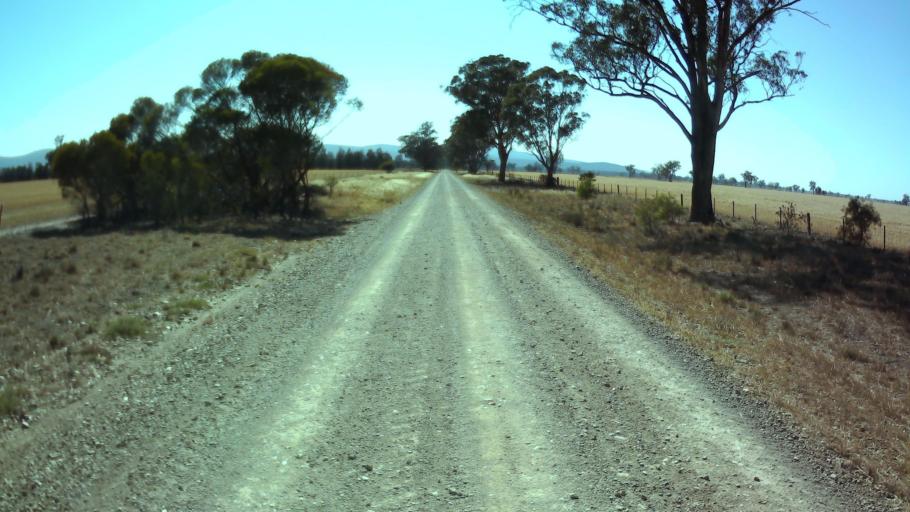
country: AU
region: New South Wales
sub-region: Weddin
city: Grenfell
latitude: -33.9422
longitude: 147.8477
